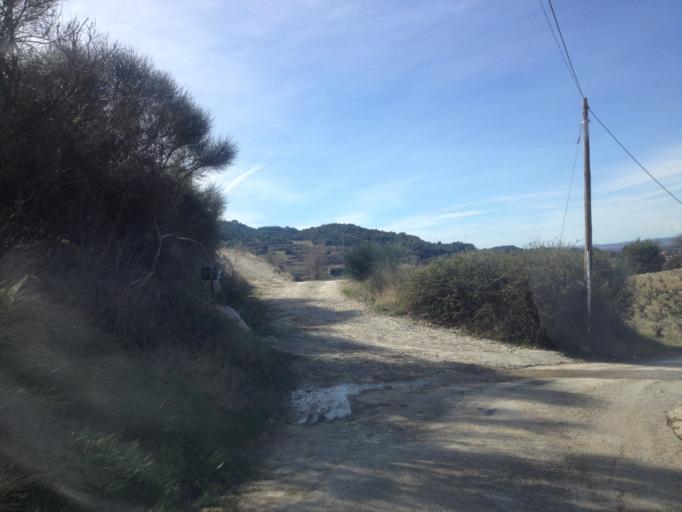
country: FR
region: Provence-Alpes-Cote d'Azur
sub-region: Departement du Vaucluse
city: Sablet
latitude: 44.1831
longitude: 5.0144
